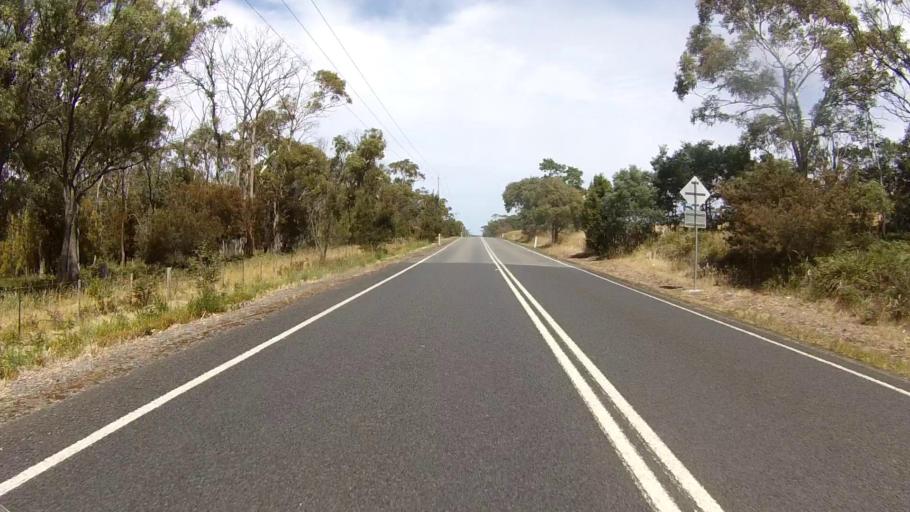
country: AU
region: Tasmania
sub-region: Clarence
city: Sandford
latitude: -43.0024
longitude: 147.4948
